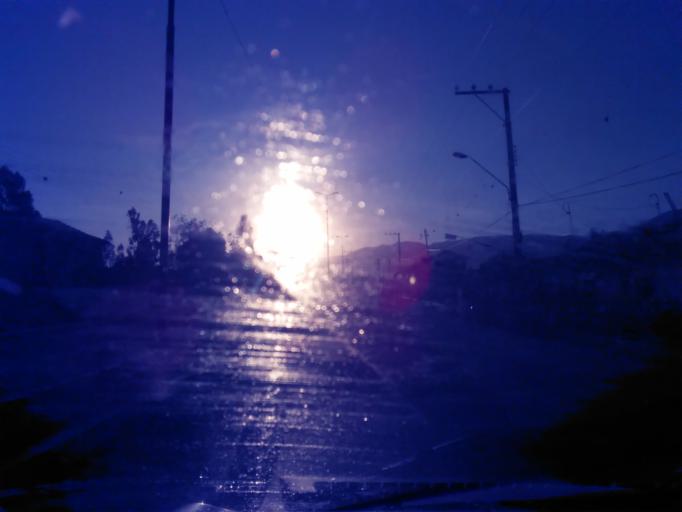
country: BO
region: Cochabamba
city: Punata
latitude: -17.5507
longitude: -65.8219
